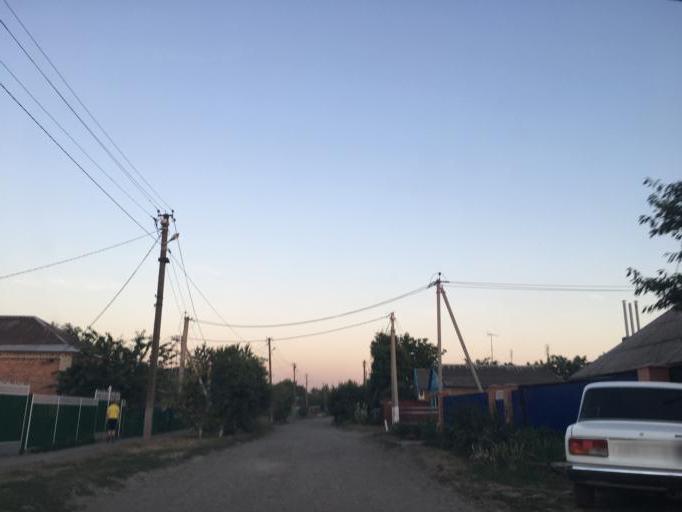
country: RU
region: Krasnodarskiy
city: Kushchevskaya
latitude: 46.5641
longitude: 39.6407
